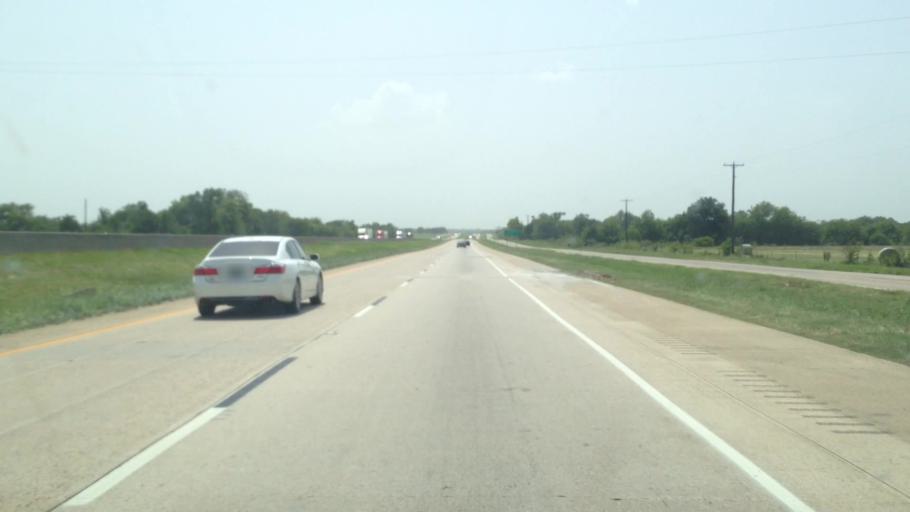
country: US
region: Texas
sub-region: Hopkins County
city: Sulphur Springs
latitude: 33.1210
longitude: -95.6845
